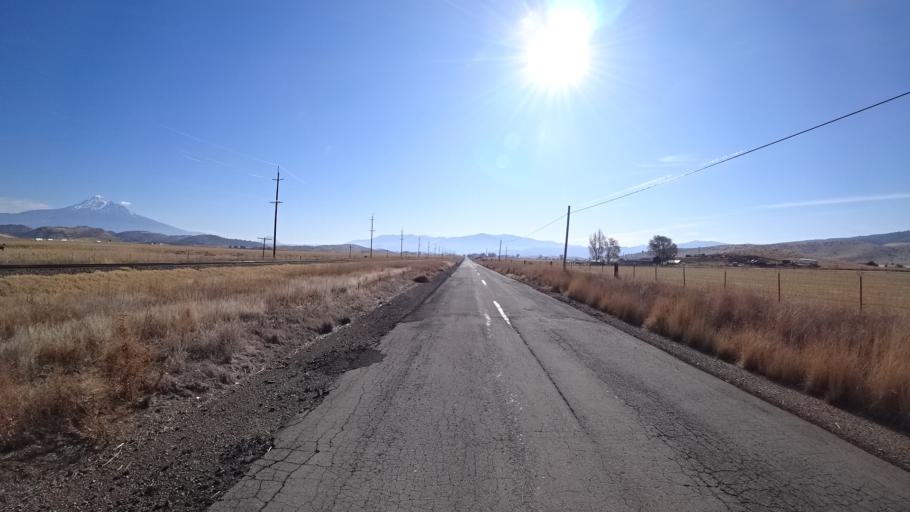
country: US
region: California
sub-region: Siskiyou County
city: Montague
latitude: 41.6157
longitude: -122.5228
